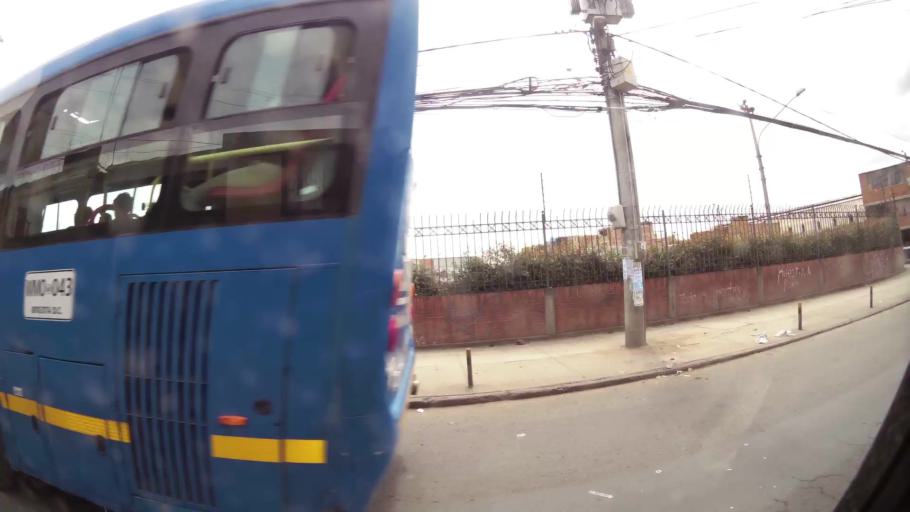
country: CO
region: Cundinamarca
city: Funza
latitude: 4.7075
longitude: -74.1379
